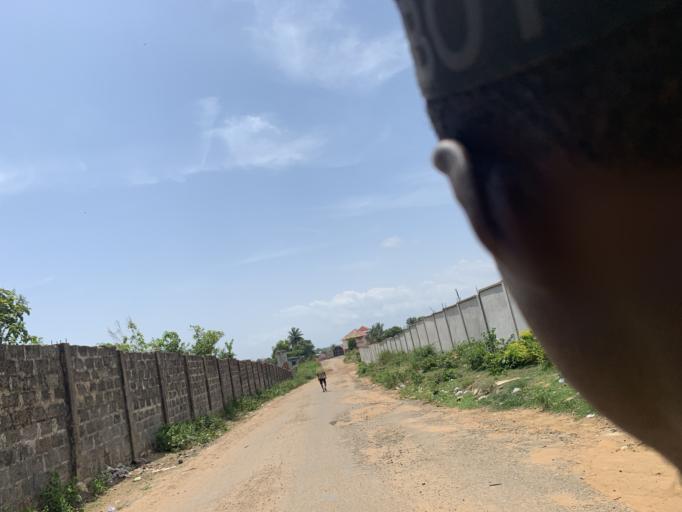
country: SL
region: Western Area
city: Waterloo
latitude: 8.3390
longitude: -13.0327
